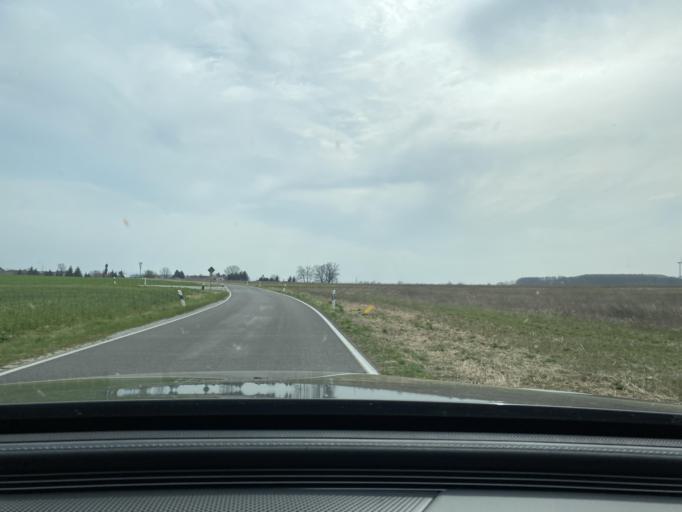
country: DE
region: Saxony
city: Neschwitz
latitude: 51.2582
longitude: 14.3323
